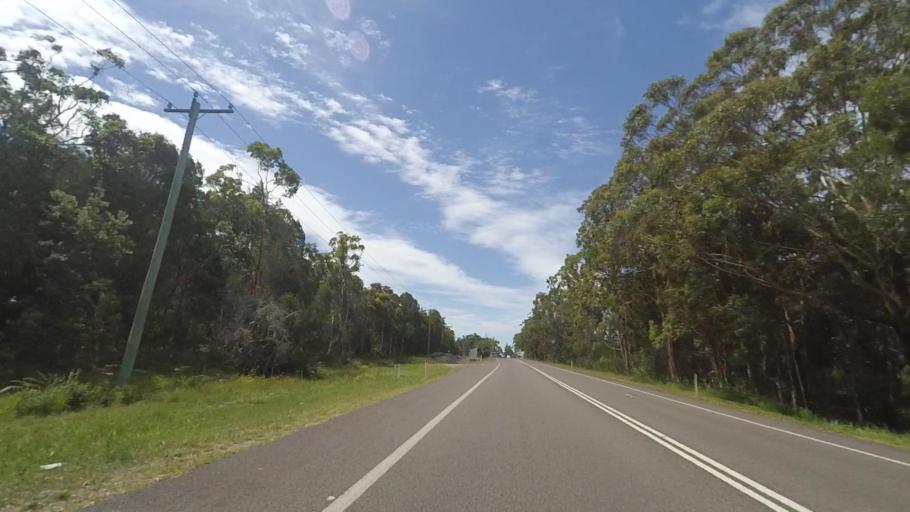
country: AU
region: New South Wales
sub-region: Port Stephens Shire
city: Anna Bay
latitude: -32.7559
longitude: 152.0682
